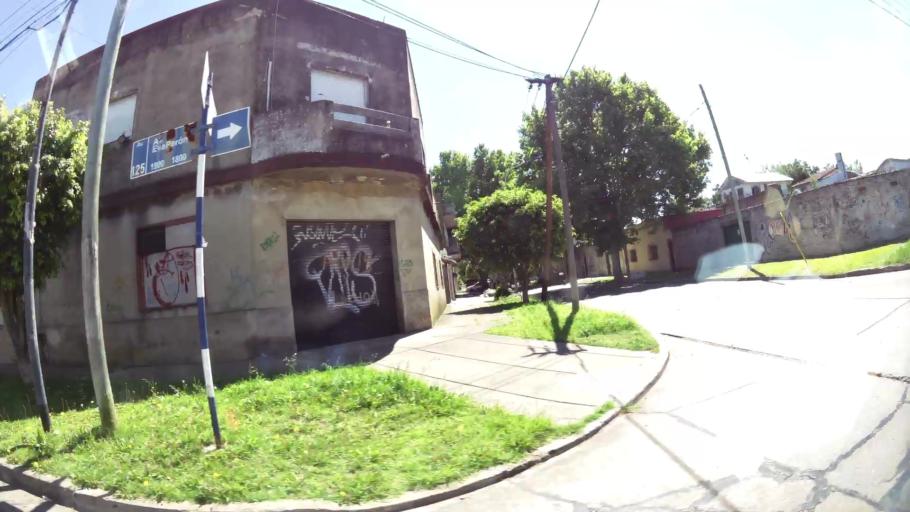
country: AR
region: Buenos Aires
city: Caseros
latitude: -34.5895
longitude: -58.5486
